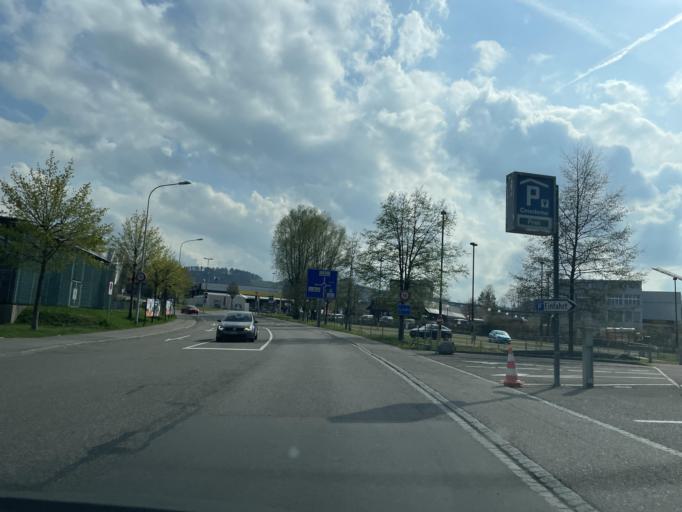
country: CH
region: Saint Gallen
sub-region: Wahlkreis St. Gallen
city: Andwil
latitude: 47.4155
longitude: 9.3120
